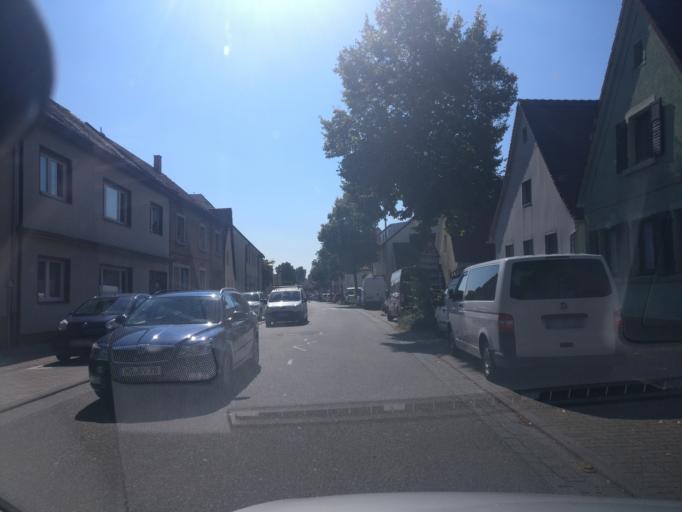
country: DE
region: Baden-Wuerttemberg
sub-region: Karlsruhe Region
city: Karlsruhe
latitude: 49.0325
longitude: 8.4595
